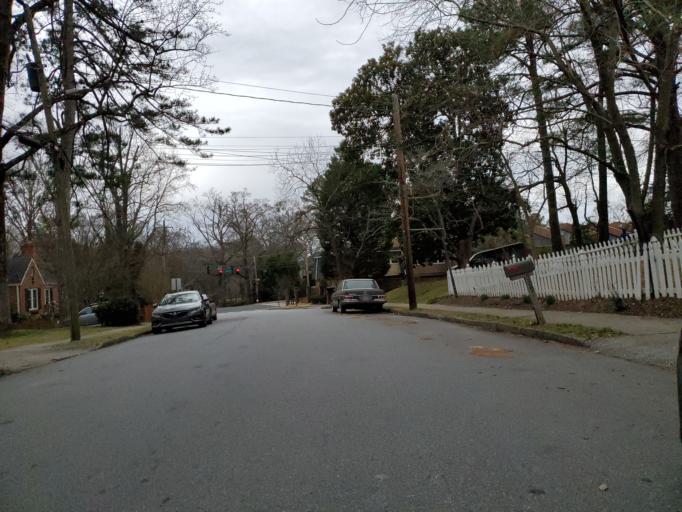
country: US
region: Georgia
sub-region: DeKalb County
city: North Decatur
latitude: 33.7872
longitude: -84.2990
